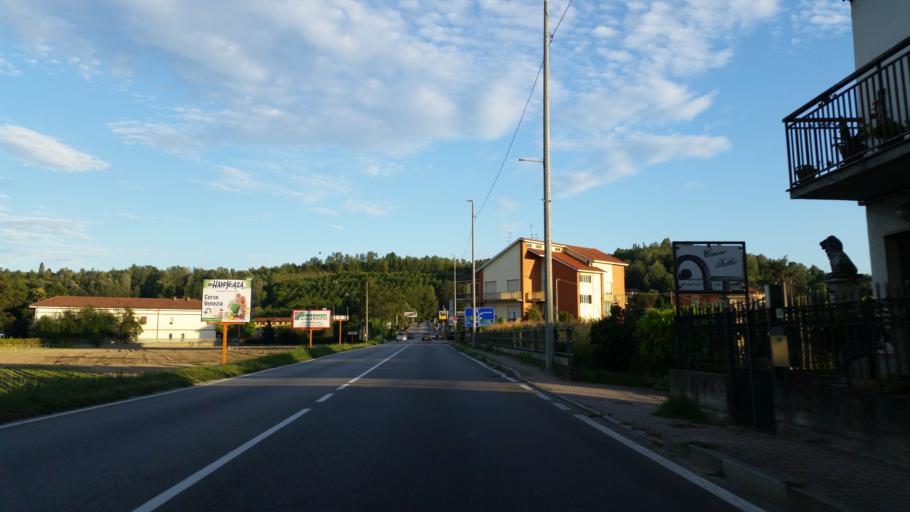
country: IT
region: Piedmont
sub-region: Provincia di Asti
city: Asti
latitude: 44.8788
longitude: 8.2142
